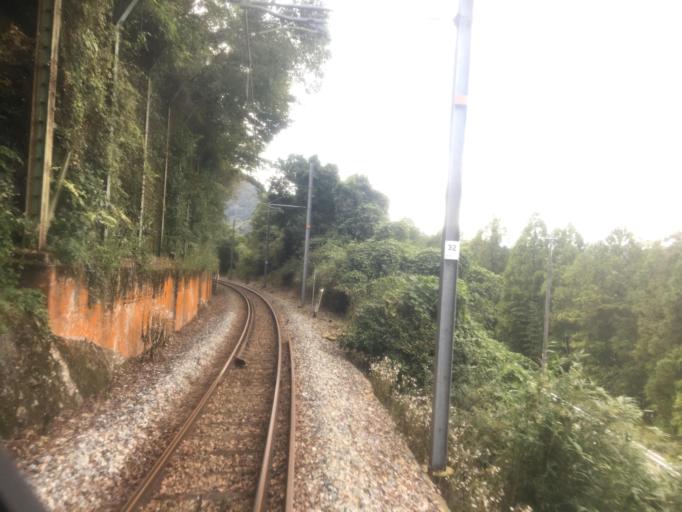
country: JP
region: Hyogo
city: Nishiwaki
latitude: 35.0704
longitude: 135.0195
